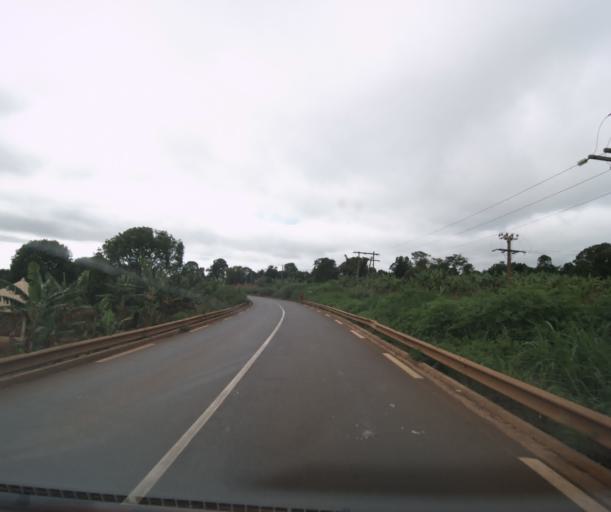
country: CM
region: West
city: Bansoa
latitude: 5.5322
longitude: 10.3293
